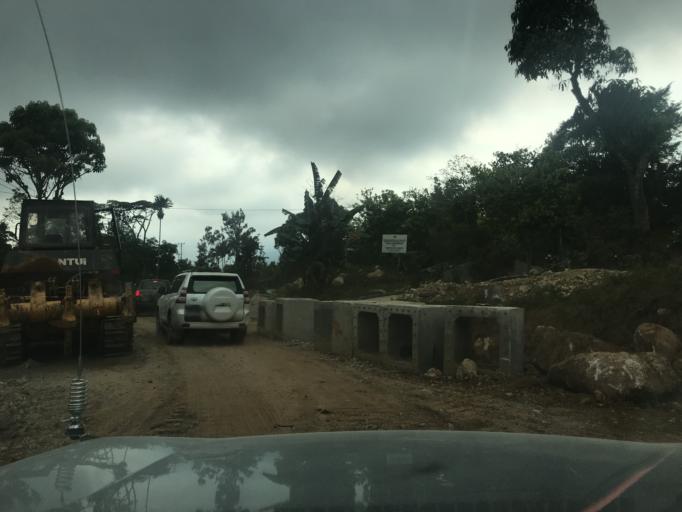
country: TL
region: Ainaro
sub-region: Ainaro
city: Ainaro
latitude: -8.9974
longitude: 125.5043
